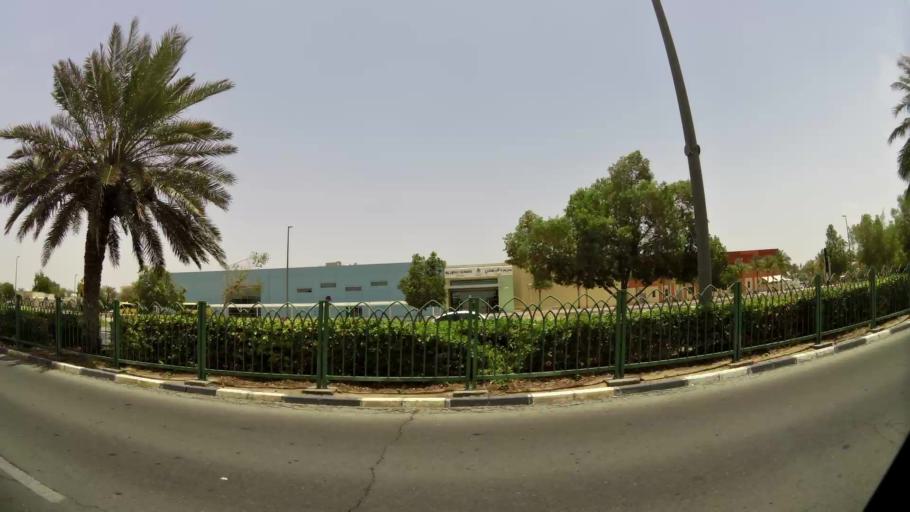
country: AE
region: Abu Dhabi
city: Al Ain
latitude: 24.2088
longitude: 55.7465
